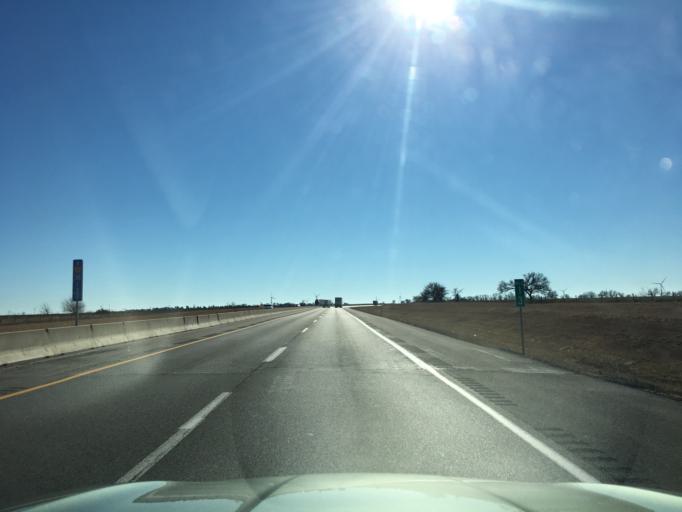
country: US
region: Kansas
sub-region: Sumner County
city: Wellington
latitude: 37.1872
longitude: -97.3409
